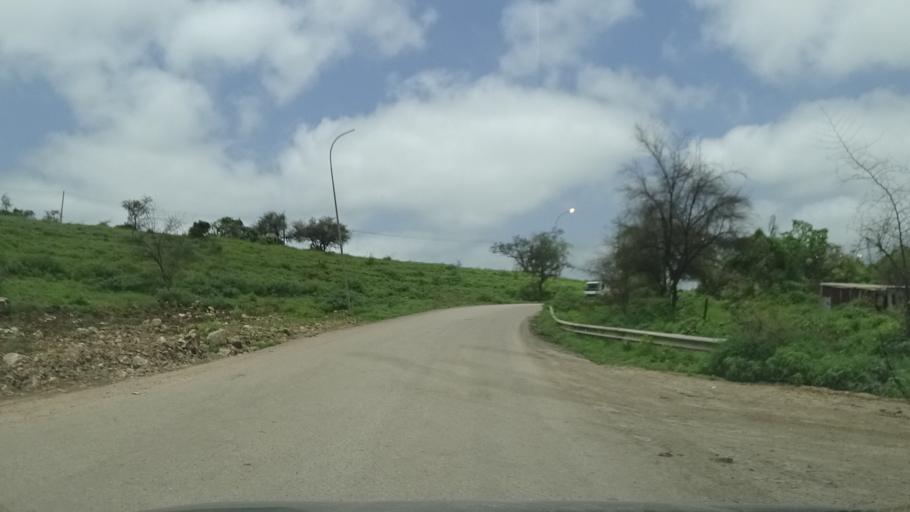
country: OM
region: Zufar
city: Salalah
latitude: 17.1817
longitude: 54.1593
